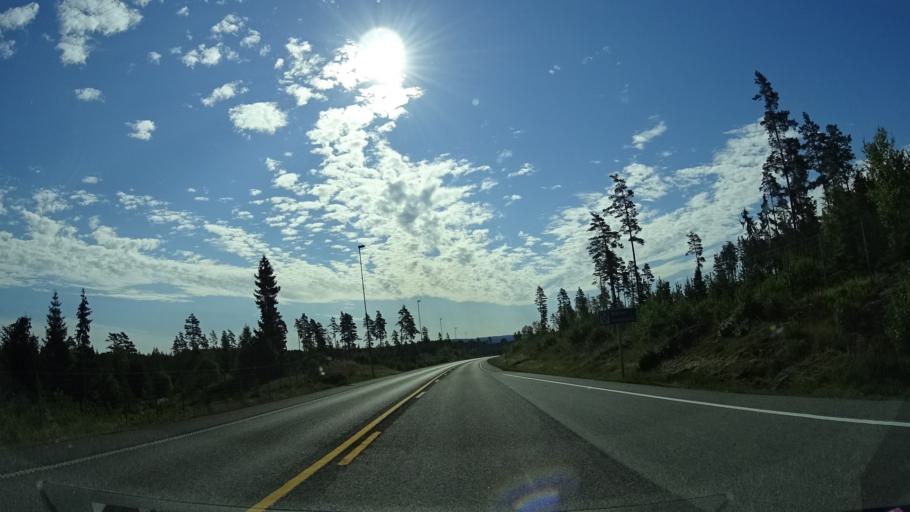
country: NO
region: Ostfold
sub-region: Marker
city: Orje
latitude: 59.5390
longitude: 11.5439
